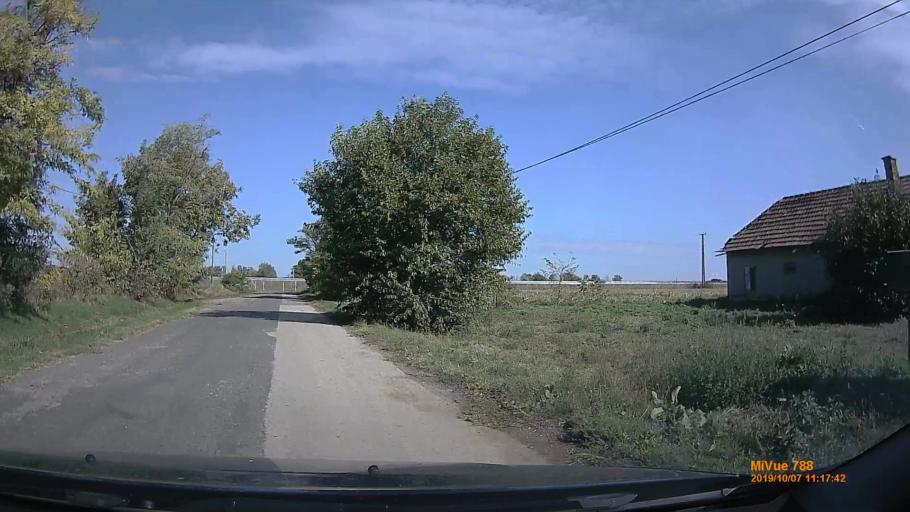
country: HU
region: Bekes
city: Kondoros
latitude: 46.7376
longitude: 20.7842
